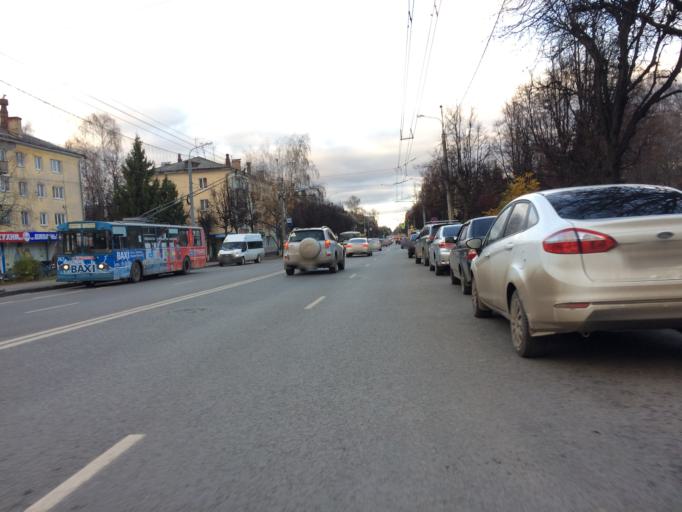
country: RU
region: Mariy-El
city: Yoshkar-Ola
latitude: 56.6356
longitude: 47.8855
